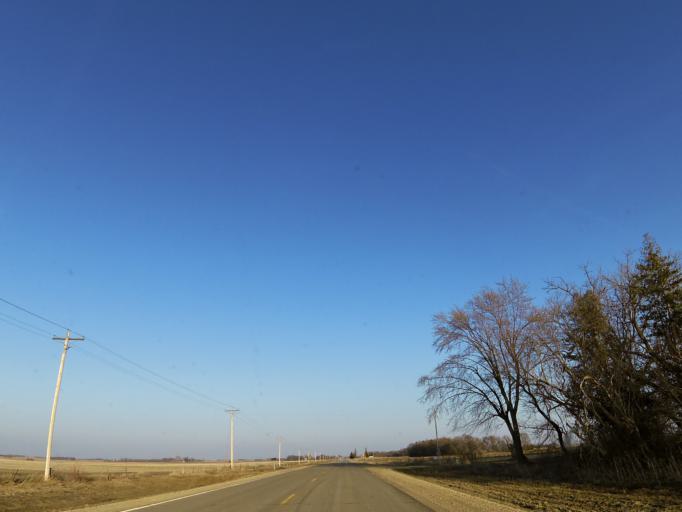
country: US
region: Iowa
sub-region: Worth County
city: Northwood
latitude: 43.4389
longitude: -93.1142
